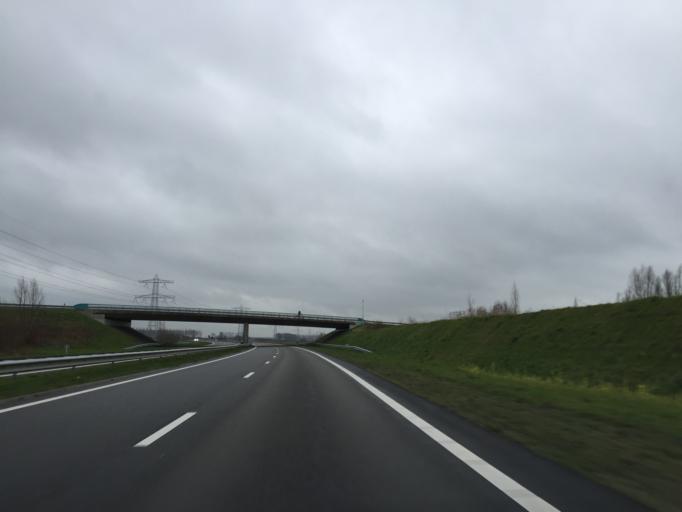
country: NL
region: Zeeland
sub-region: Gemeente Terneuzen
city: Terneuzen
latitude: 51.3165
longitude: 3.7965
